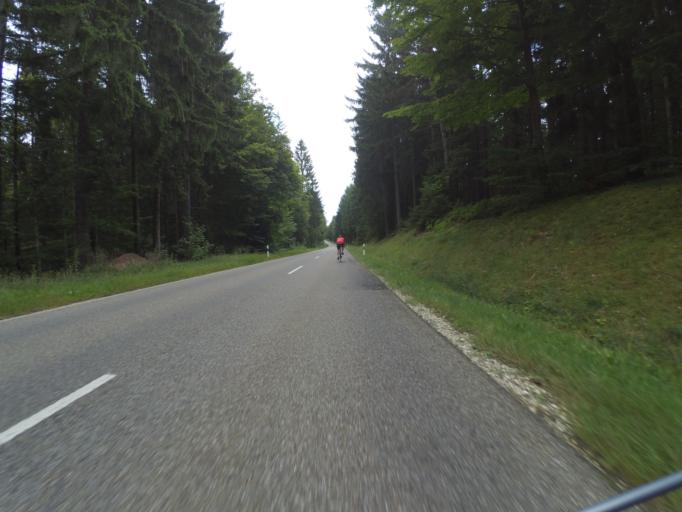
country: DE
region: Baden-Wuerttemberg
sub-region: Freiburg Region
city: Bonndorf im Schwarzwald
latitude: 47.8197
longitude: 8.3108
